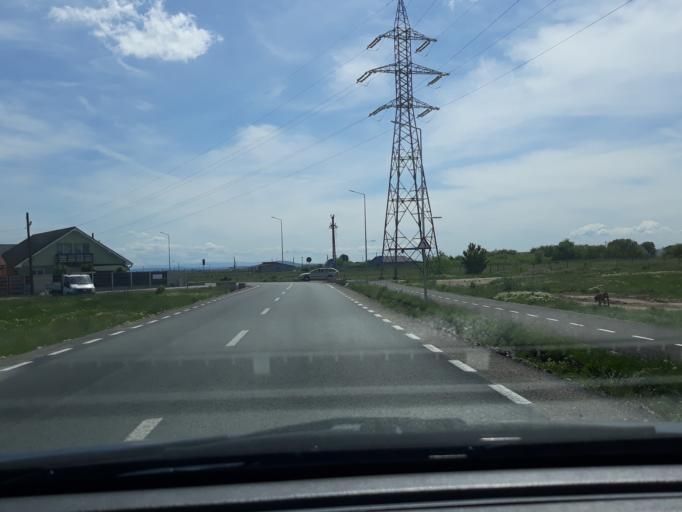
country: RO
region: Bihor
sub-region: Comuna Santandrei
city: Santandrei
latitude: 47.0680
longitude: 21.8622
